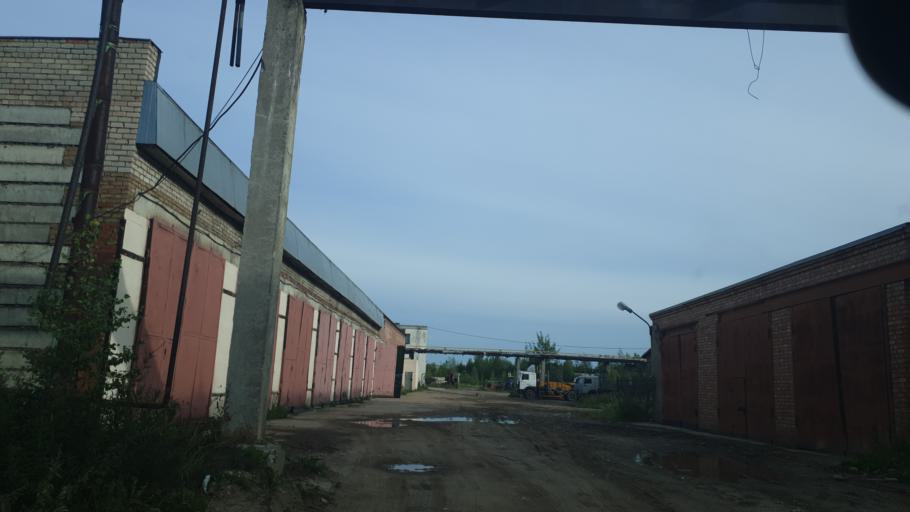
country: RU
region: Komi Republic
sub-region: Syktyvdinskiy Rayon
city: Syktyvkar
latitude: 61.7232
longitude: 50.7537
